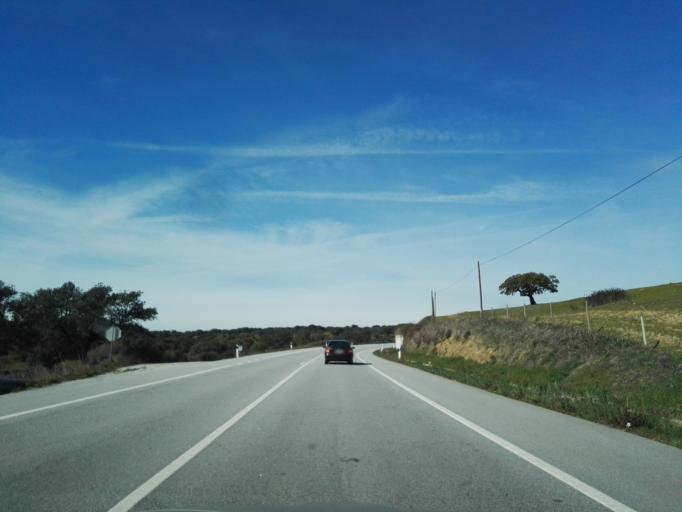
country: PT
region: Portalegre
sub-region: Portalegre
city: Alegrete
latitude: 39.1804
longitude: -7.3433
